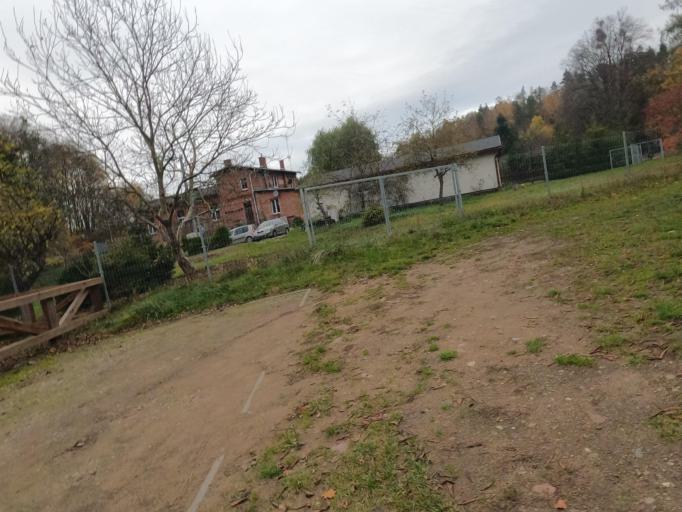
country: PL
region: Pomeranian Voivodeship
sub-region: Powiat starogardzki
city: Skarszewy
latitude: 54.0414
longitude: 18.4522
